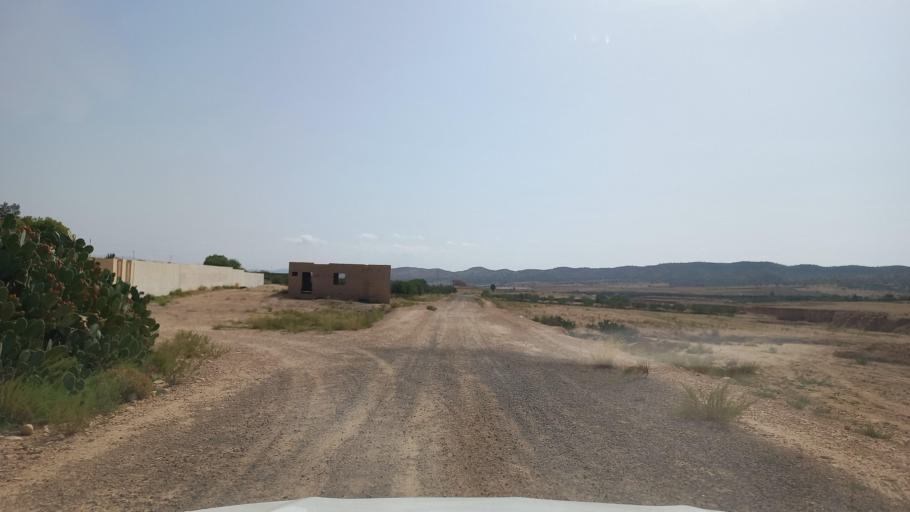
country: TN
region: Al Qasrayn
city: Sbiba
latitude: 35.3934
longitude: 8.9546
